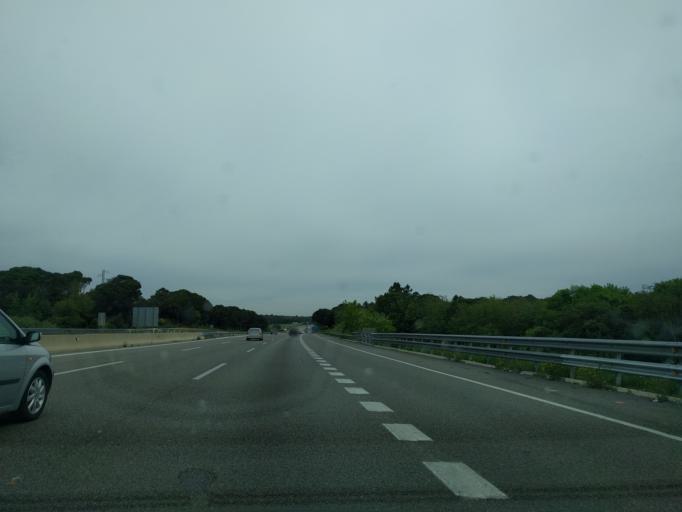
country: ES
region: Catalonia
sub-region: Provincia de Girona
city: Aiguaviva
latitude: 41.9086
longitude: 2.7730
